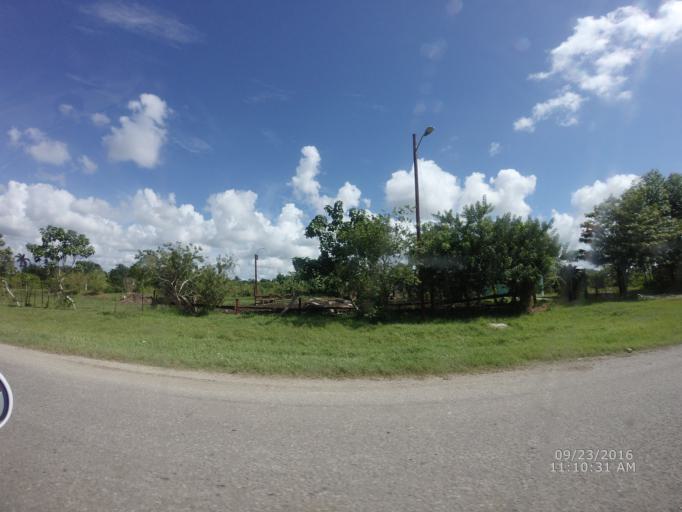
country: CU
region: La Habana
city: Arroyo Naranjo
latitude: 23.0209
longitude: -82.2572
